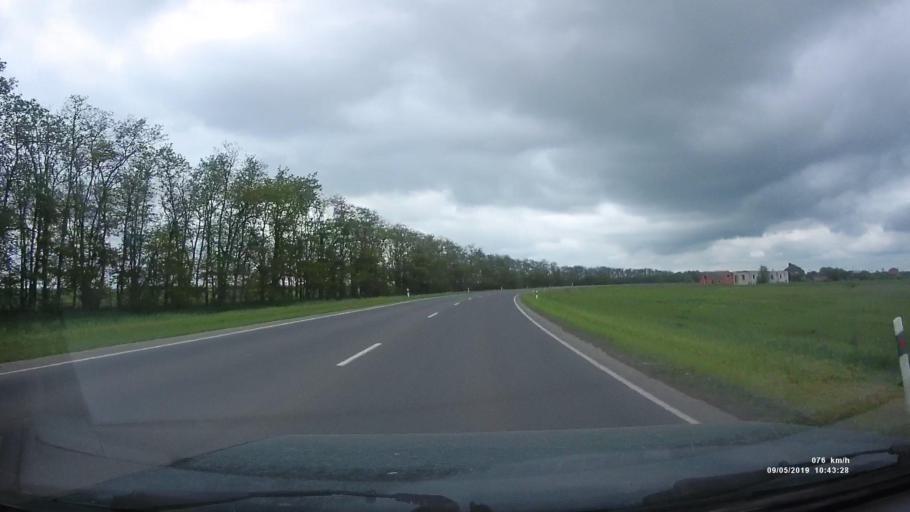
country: RU
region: Rostov
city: Peshkovo
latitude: 47.0079
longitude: 39.4031
